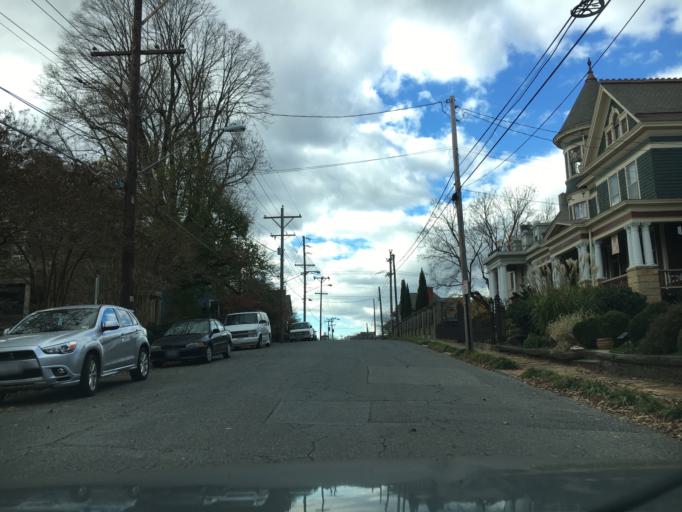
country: US
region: Virginia
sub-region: City of Lynchburg
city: Lynchburg
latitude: 37.4091
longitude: -79.1413
